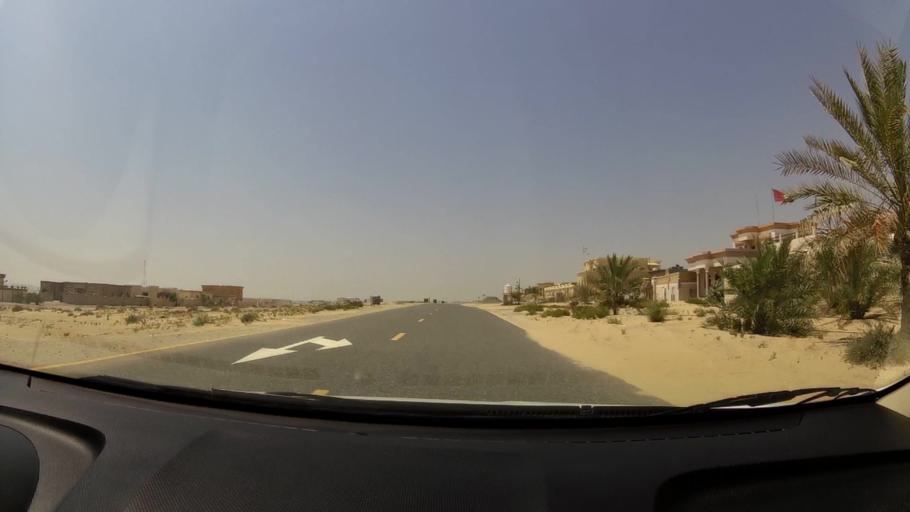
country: AE
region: Umm al Qaywayn
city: Umm al Qaywayn
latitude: 25.5081
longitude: 55.5832
